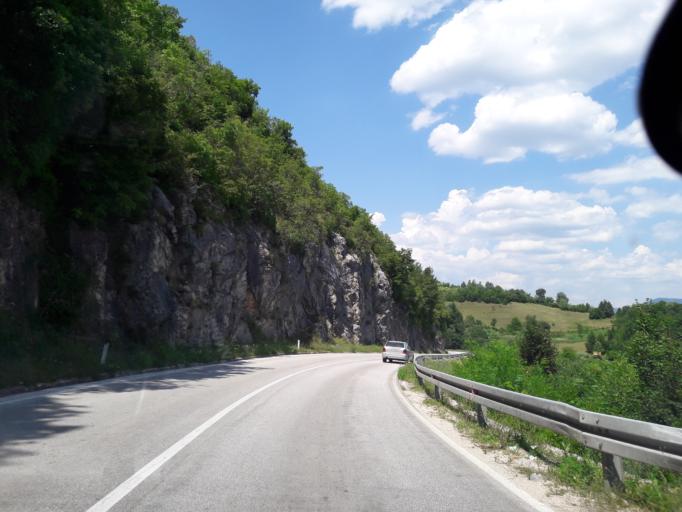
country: BA
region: Republika Srpska
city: Mrkonjic Grad
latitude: 44.4156
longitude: 17.0984
